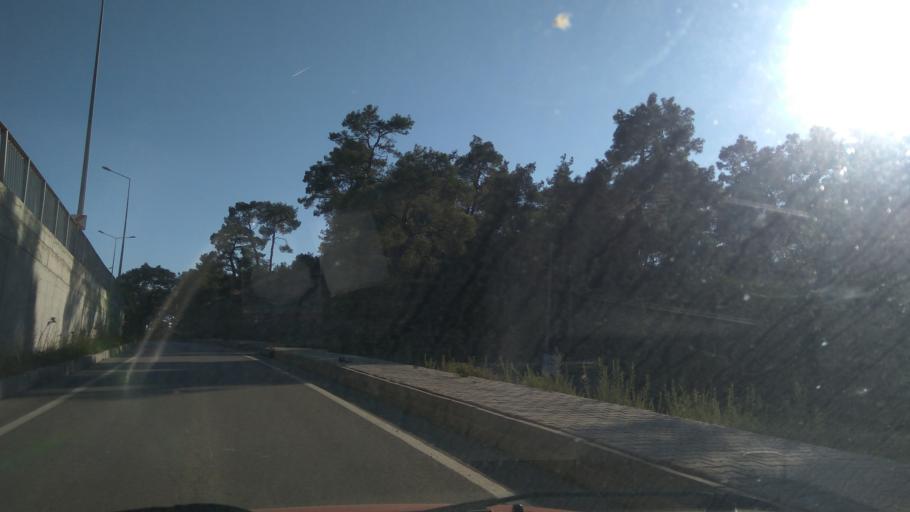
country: TR
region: Antalya
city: Kemer
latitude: 36.5902
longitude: 30.5407
